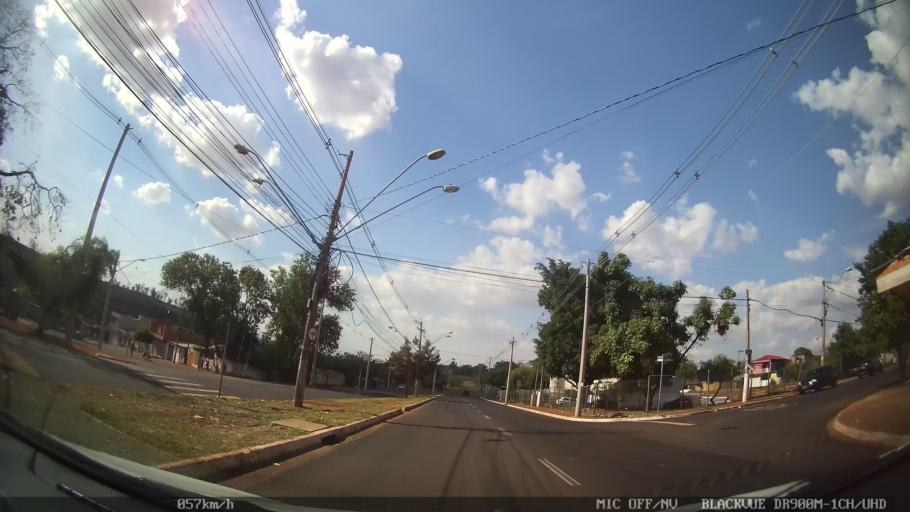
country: BR
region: Sao Paulo
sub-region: Ribeirao Preto
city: Ribeirao Preto
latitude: -21.1969
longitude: -47.8520
